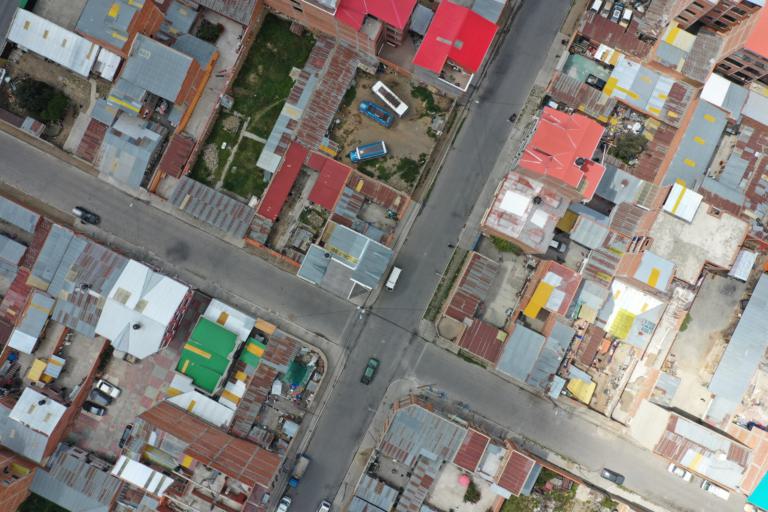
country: BO
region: La Paz
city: La Paz
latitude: -16.5227
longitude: -68.1569
